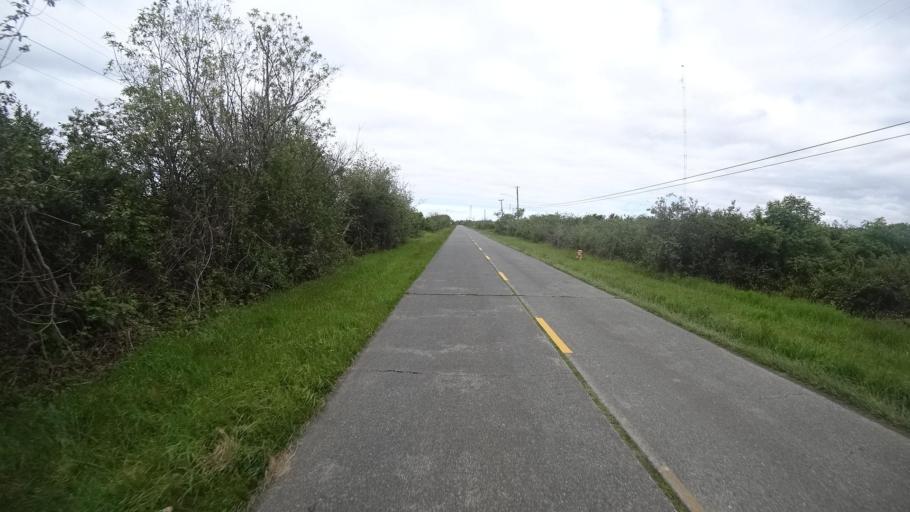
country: US
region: California
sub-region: Humboldt County
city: Arcata
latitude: 40.8526
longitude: -124.0847
